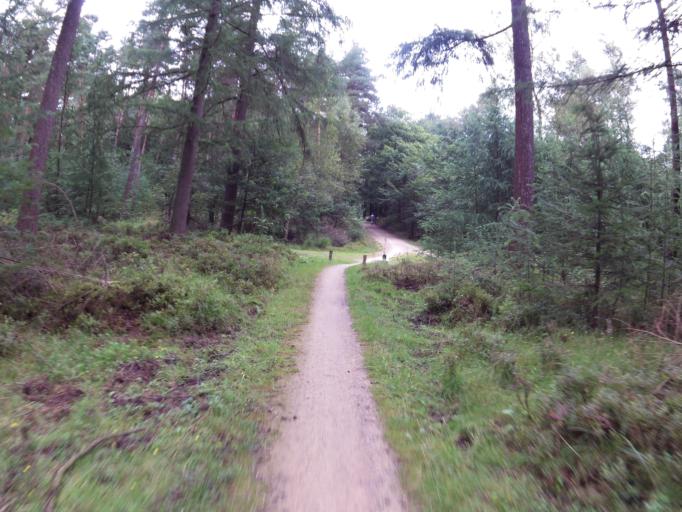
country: NL
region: Gelderland
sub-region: Gemeente Apeldoorn
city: Loenen
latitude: 52.0902
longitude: 6.0055
